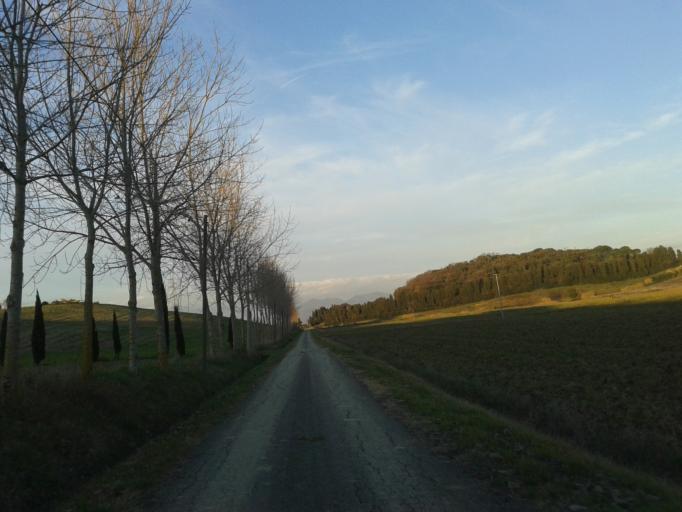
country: IT
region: Tuscany
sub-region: Provincia di Livorno
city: Guasticce
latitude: 43.5871
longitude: 10.4088
